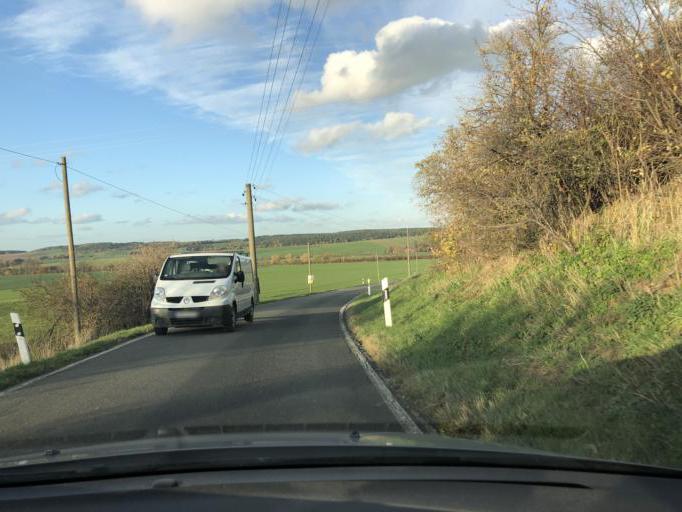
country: DE
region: Thuringia
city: Dreitzsch
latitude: 50.7283
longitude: 11.8158
